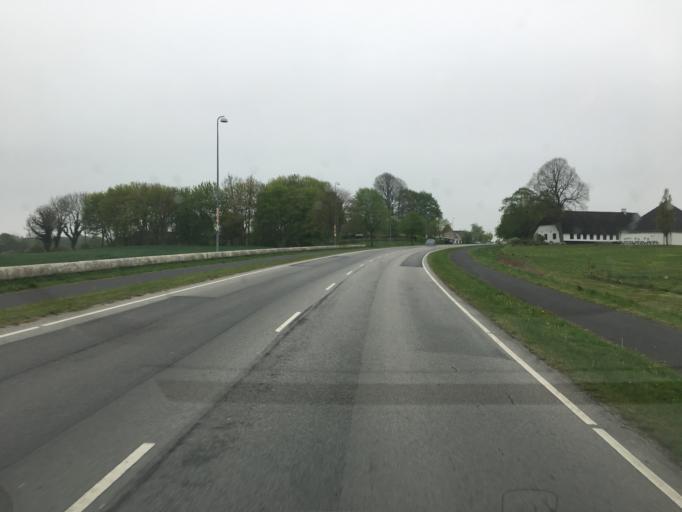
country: DK
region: South Denmark
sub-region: Aabenraa Kommune
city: Padborg
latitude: 54.8276
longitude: 9.3654
